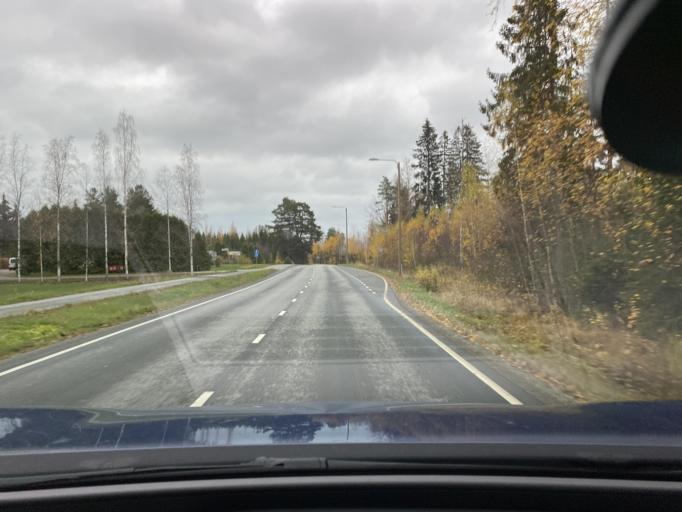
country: FI
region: Satakunta
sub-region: Pori
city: Huittinen
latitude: 61.1509
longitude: 22.6552
